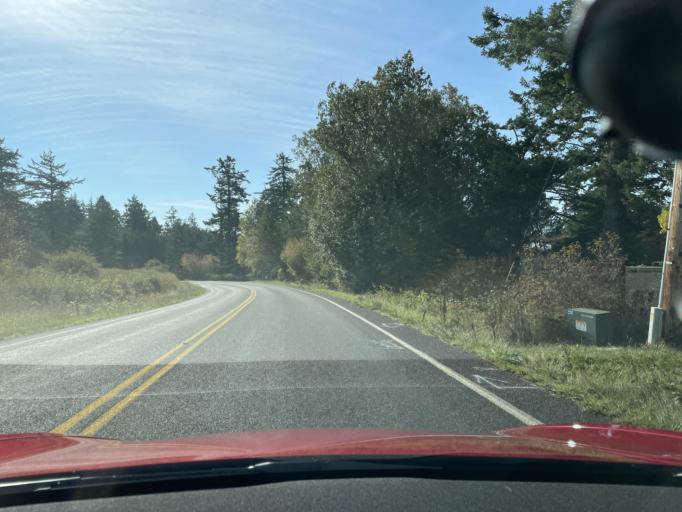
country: US
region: Washington
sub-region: San Juan County
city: Friday Harbor
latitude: 48.4723
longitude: -123.0334
